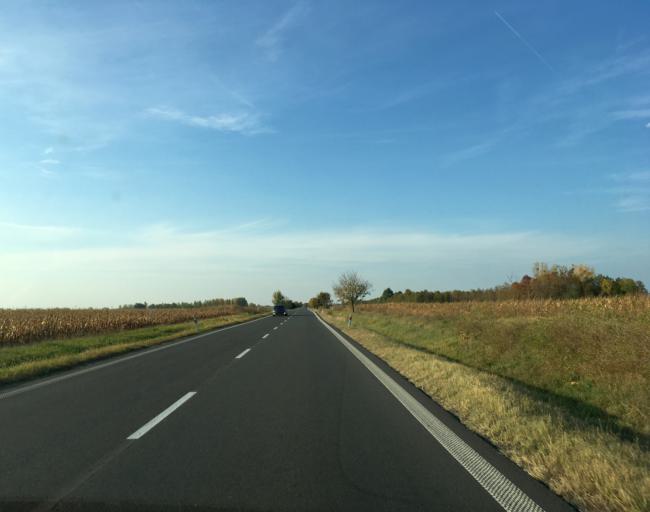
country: SK
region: Nitriansky
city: Surany
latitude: 48.0697
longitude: 18.0924
